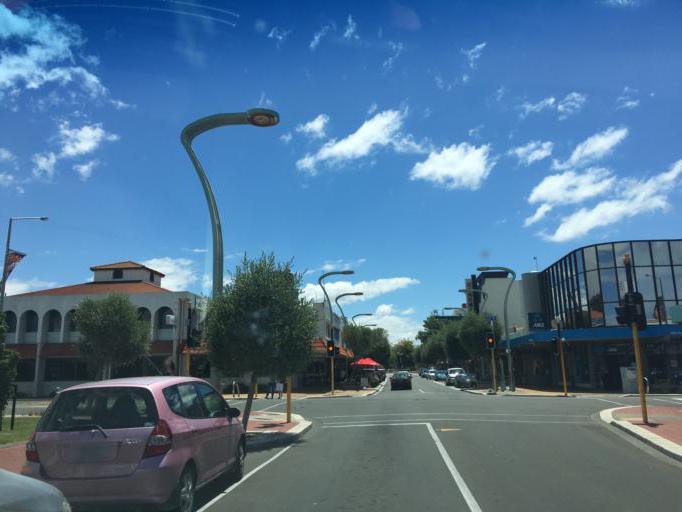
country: NZ
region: Hawke's Bay
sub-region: Hastings District
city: Hastings
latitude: -39.6431
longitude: 176.8445
